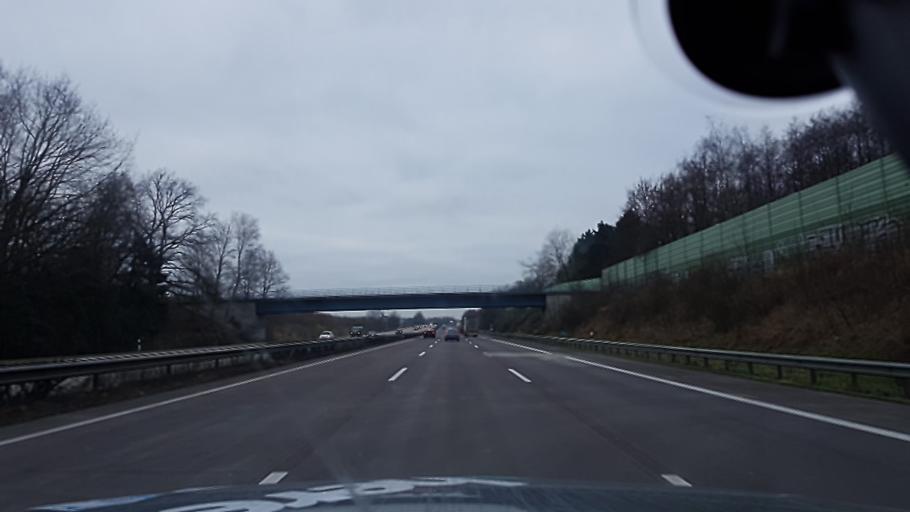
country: DE
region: Schleswig-Holstein
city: Grosshansdorf
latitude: 53.6510
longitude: 10.2904
